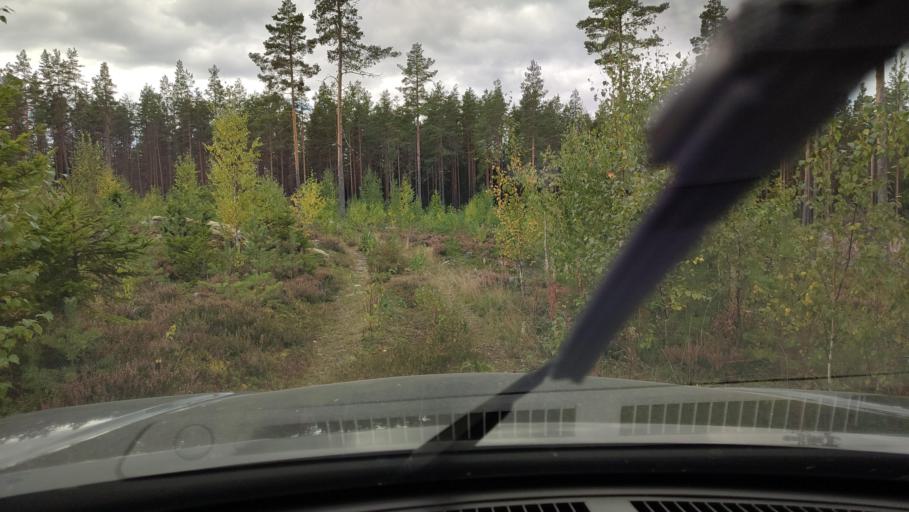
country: FI
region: Southern Ostrobothnia
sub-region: Suupohja
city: Karijoki
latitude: 62.2257
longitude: 21.6145
